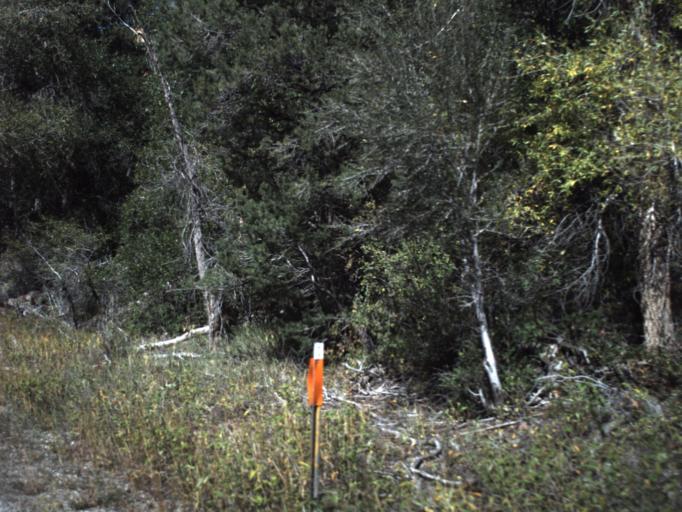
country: US
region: Utah
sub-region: Beaver County
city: Beaver
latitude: 38.2671
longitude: -112.5490
